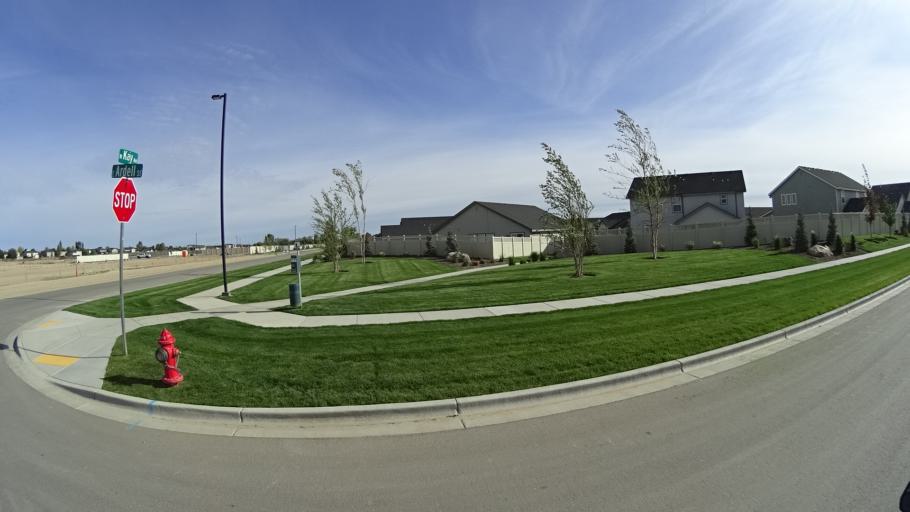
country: US
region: Idaho
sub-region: Ada County
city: Kuna
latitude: 43.5102
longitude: -116.4037
